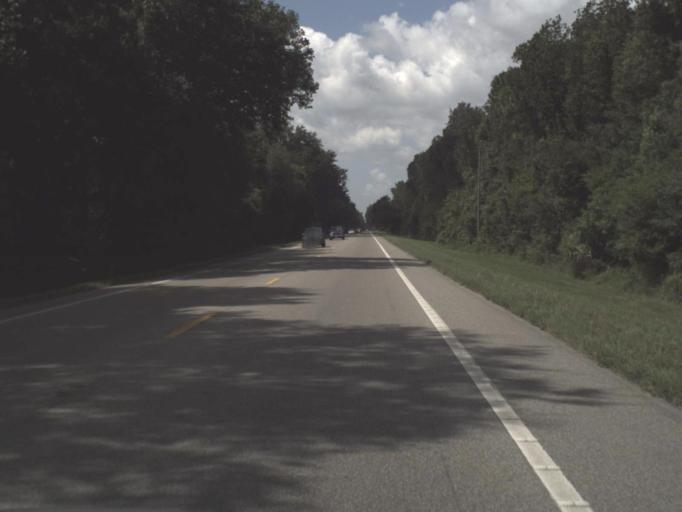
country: US
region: Florida
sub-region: Hillsborough County
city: Thonotosassa
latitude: 28.1179
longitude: -82.2417
